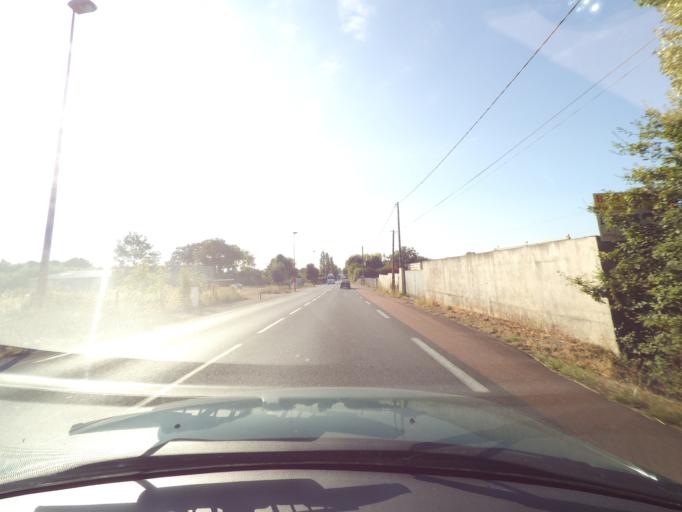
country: FR
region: Poitou-Charentes
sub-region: Departement des Deux-Sevres
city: Boisme
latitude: 46.8268
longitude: -0.4224
